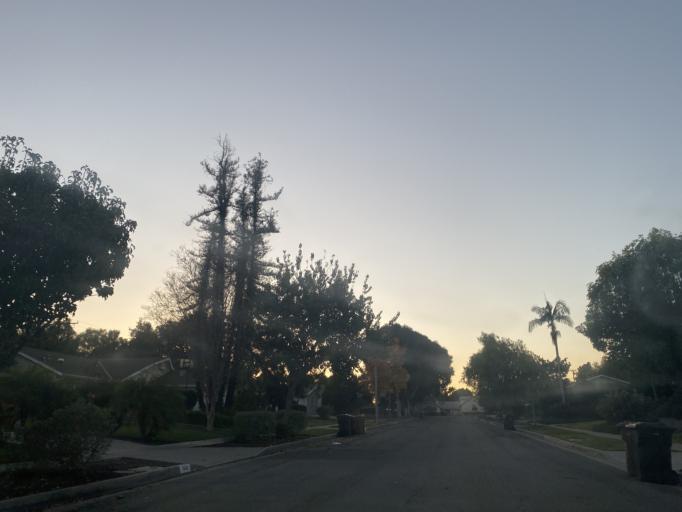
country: US
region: California
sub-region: Orange County
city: Fullerton
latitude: 33.8822
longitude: -117.9016
